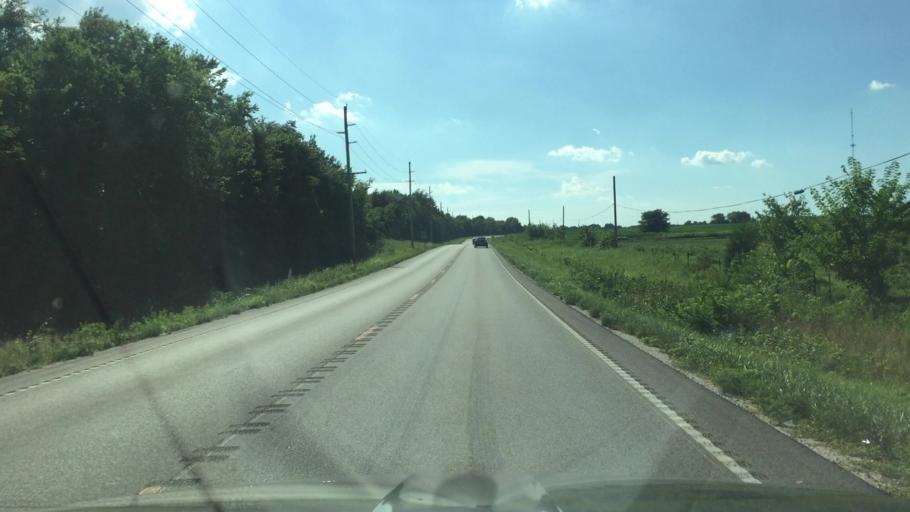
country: US
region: Missouri
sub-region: Morgan County
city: Versailles
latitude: 38.4037
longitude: -92.7536
